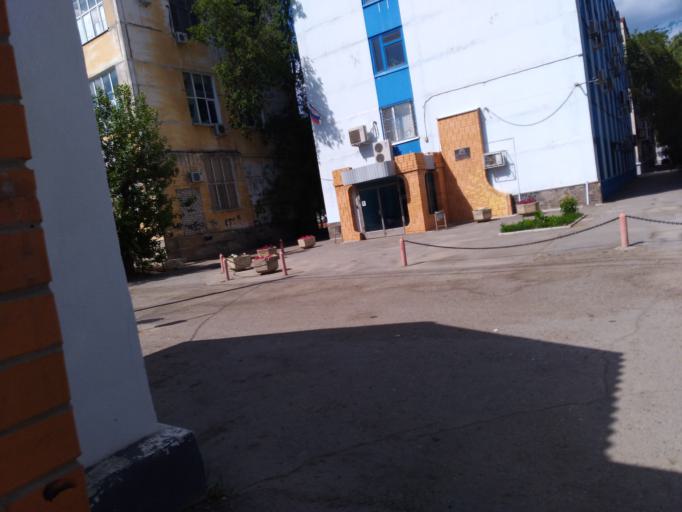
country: RU
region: Volgograd
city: Volgograd
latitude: 48.7199
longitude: 44.5357
